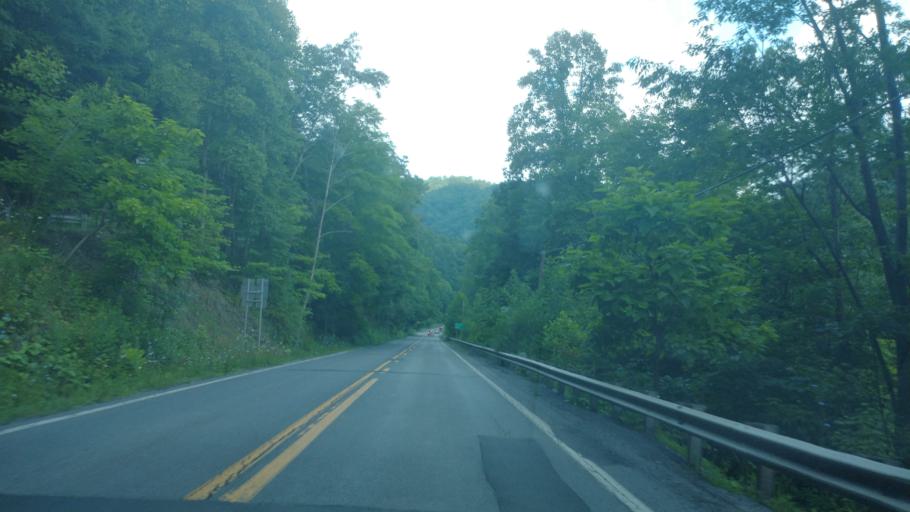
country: US
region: West Virginia
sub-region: Mercer County
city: Bluewell
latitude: 37.3849
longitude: -81.4156
